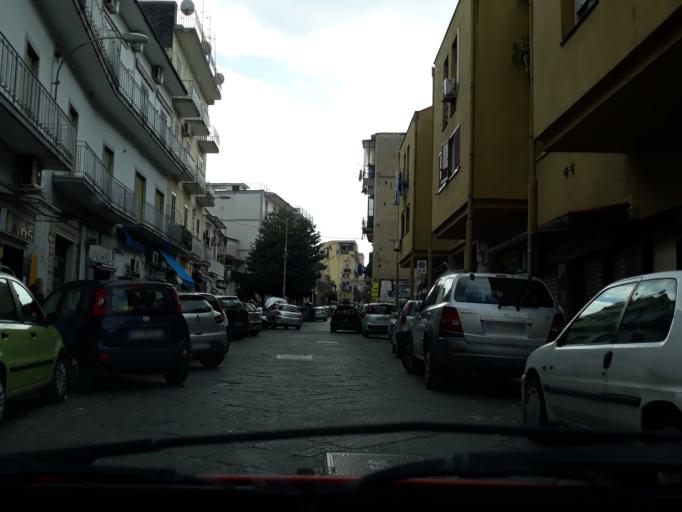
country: IT
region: Campania
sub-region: Provincia di Napoli
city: Mugnano di Napoli
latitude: 40.8895
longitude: 14.2310
